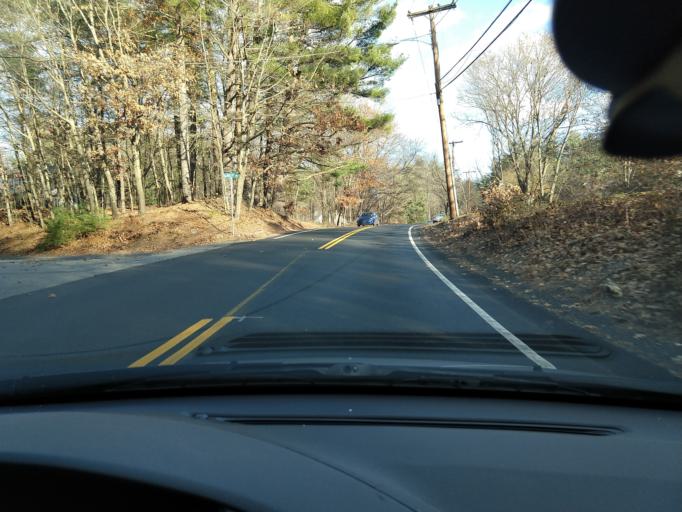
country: US
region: Massachusetts
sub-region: Middlesex County
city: Westford
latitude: 42.5519
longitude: -71.4353
